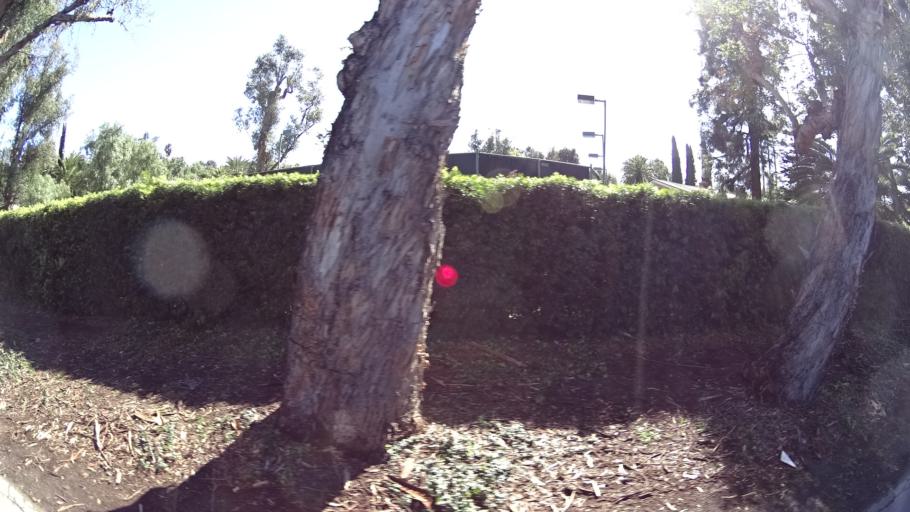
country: US
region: California
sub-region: Orange County
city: Villa Park
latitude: 33.8448
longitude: -117.8098
